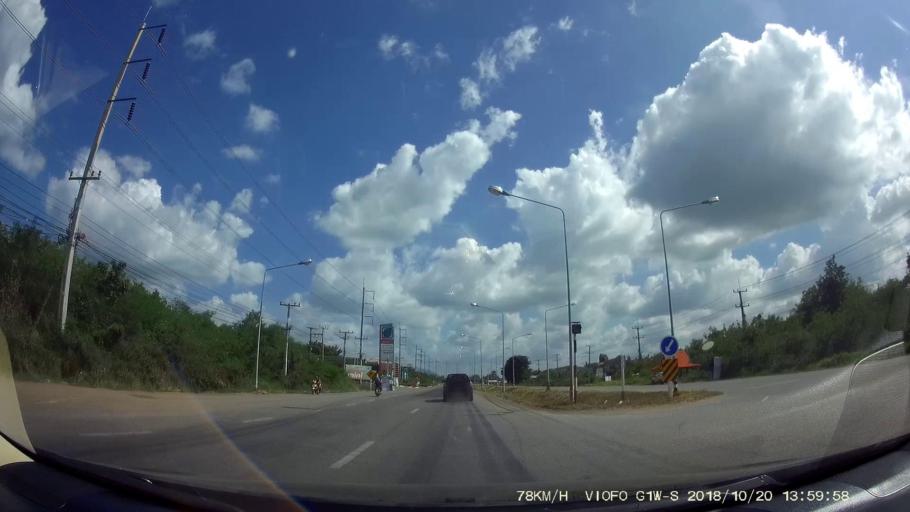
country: TH
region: Khon Kaen
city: Chum Phae
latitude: 16.5195
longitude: 102.1164
